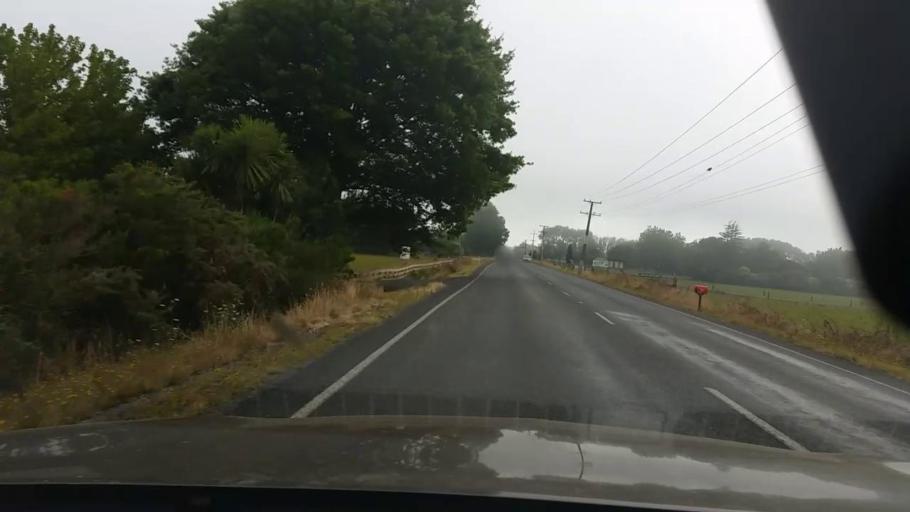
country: NZ
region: Waikato
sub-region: Hamilton City
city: Hamilton
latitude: -37.6286
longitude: 175.3166
